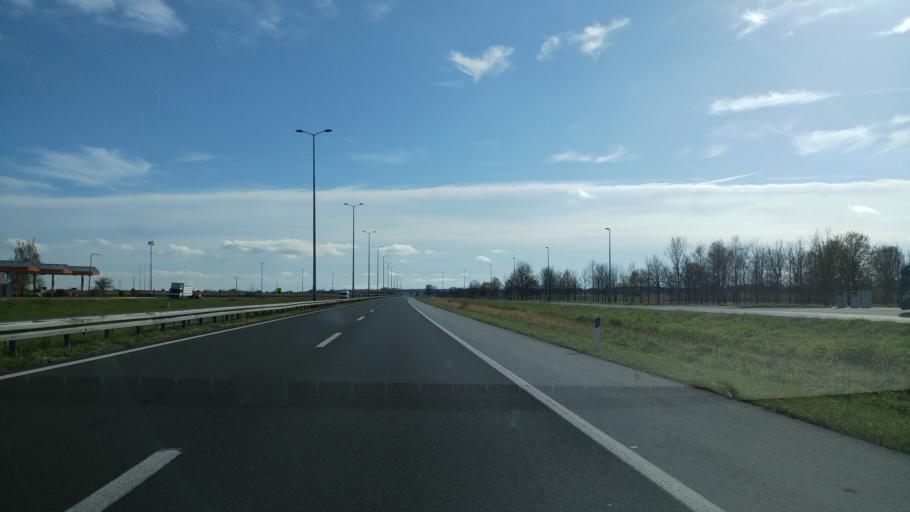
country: HR
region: Sisacko-Moslavacka
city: Lipovljani
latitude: 45.4021
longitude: 16.8601
